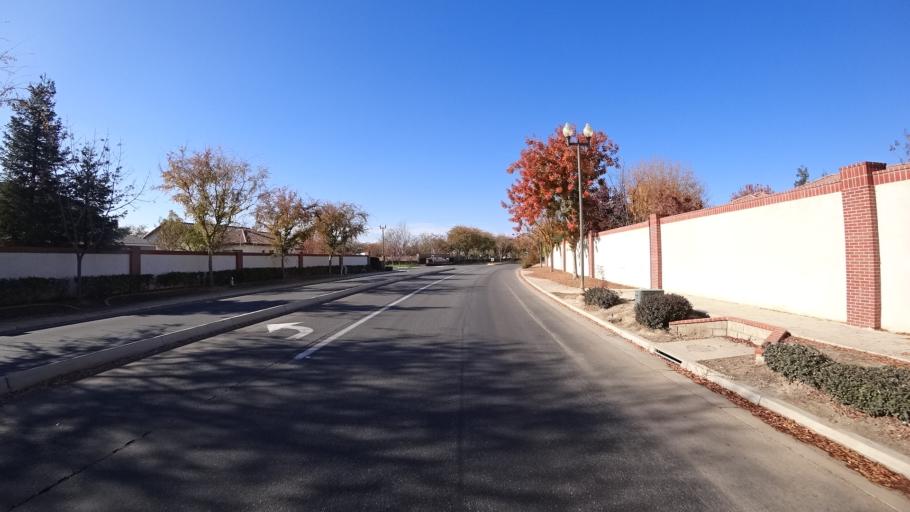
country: US
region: California
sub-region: Kern County
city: Rosedale
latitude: 35.3277
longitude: -119.1399
